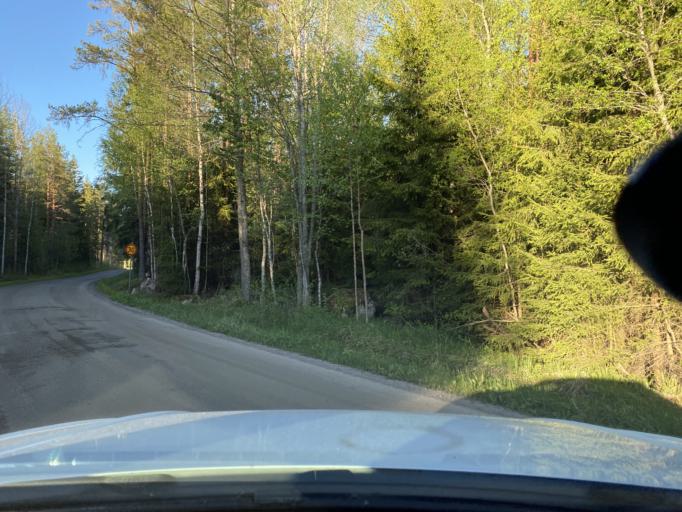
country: FI
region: Satakunta
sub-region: Rauma
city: Lappi
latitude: 61.1466
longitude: 21.9085
